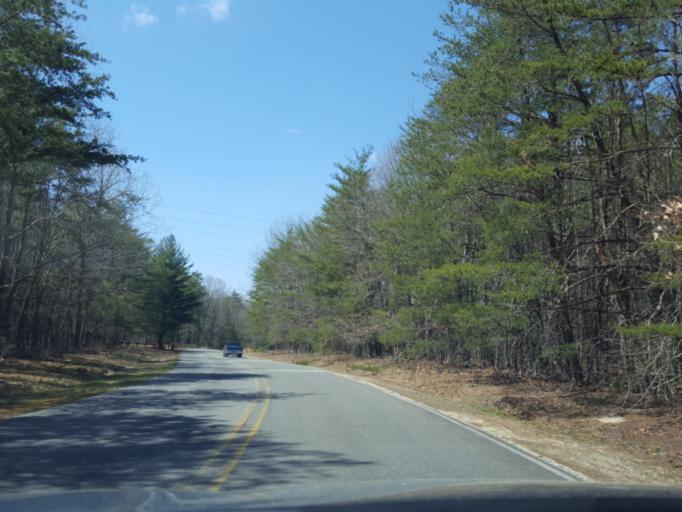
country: US
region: Maryland
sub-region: Prince George's County
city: Brandywine
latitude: 38.6517
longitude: -76.8310
